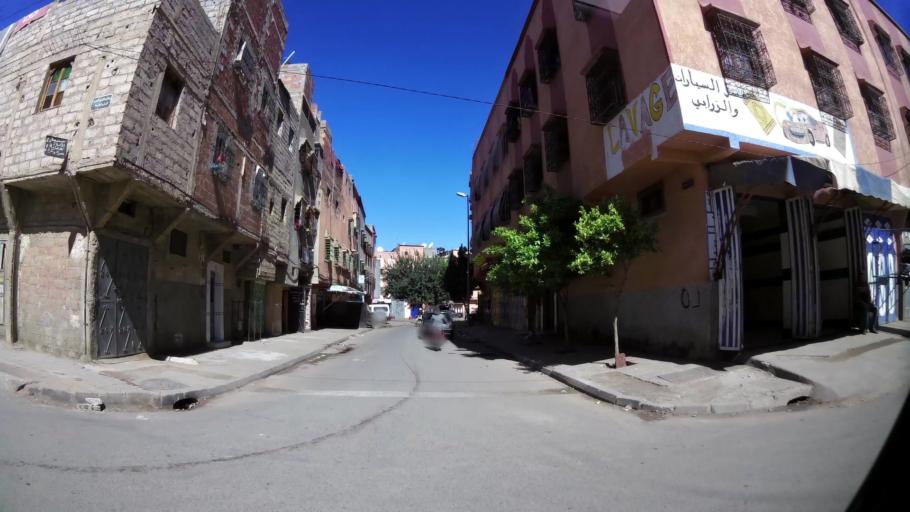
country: MA
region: Marrakech-Tensift-Al Haouz
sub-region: Marrakech
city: Marrakesh
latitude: 31.6482
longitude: -7.9832
